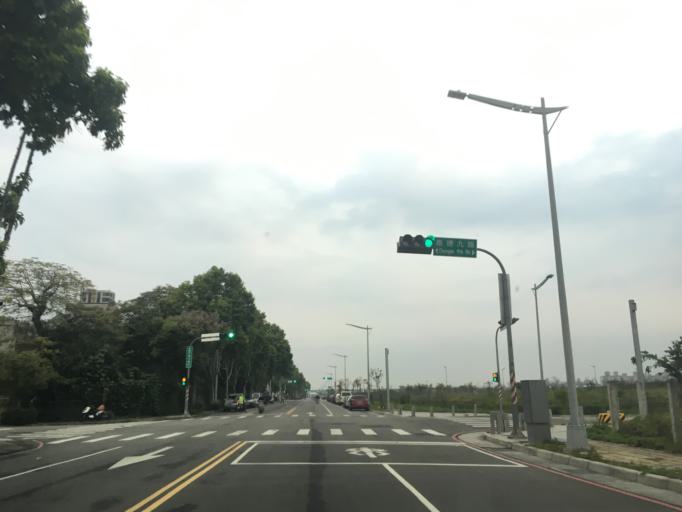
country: TW
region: Taiwan
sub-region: Taichung City
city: Taichung
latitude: 24.1866
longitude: 120.6904
